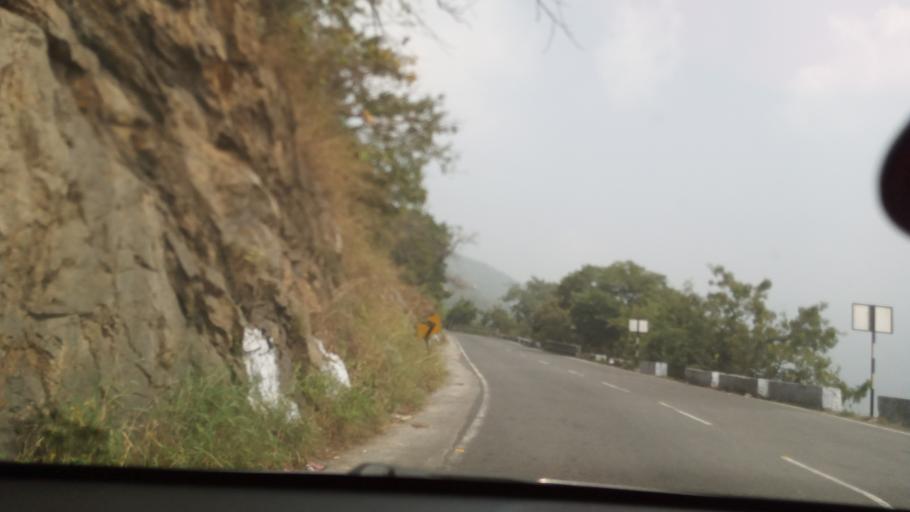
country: IN
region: Tamil Nadu
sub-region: Erode
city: Sathyamangalam
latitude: 11.5924
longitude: 77.1269
